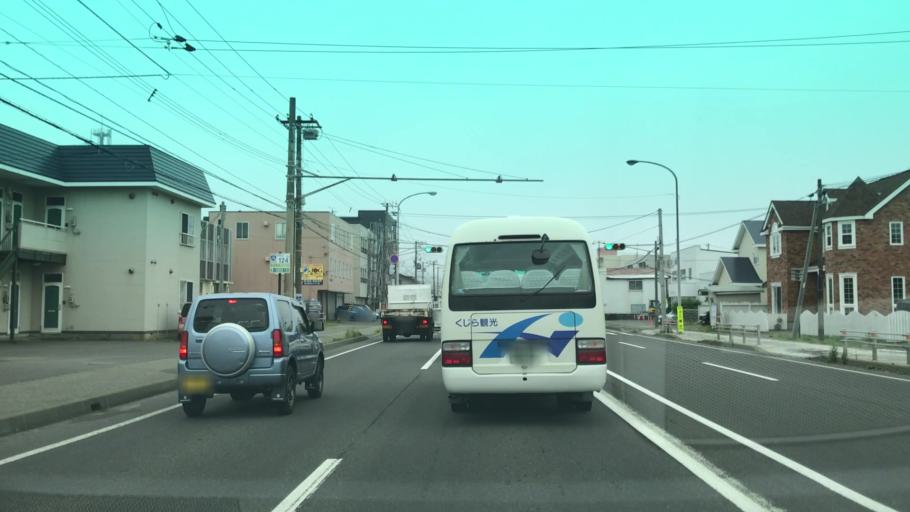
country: JP
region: Hokkaido
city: Muroran
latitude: 42.3598
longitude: 141.0531
